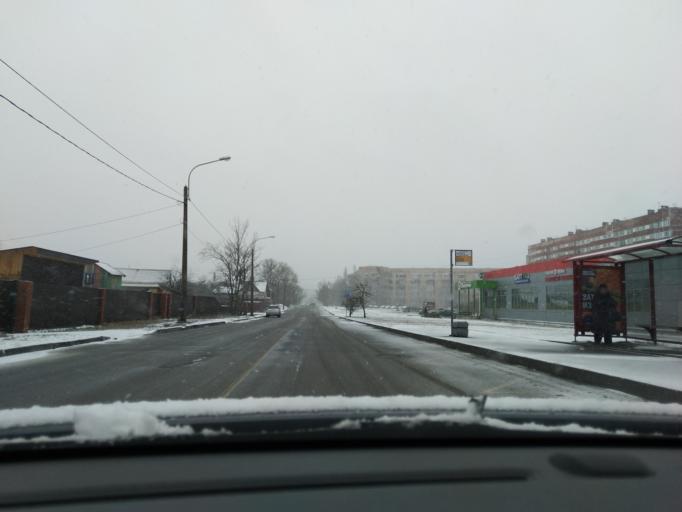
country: RU
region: St.-Petersburg
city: Krasnoye Selo
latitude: 59.7461
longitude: 30.0917
